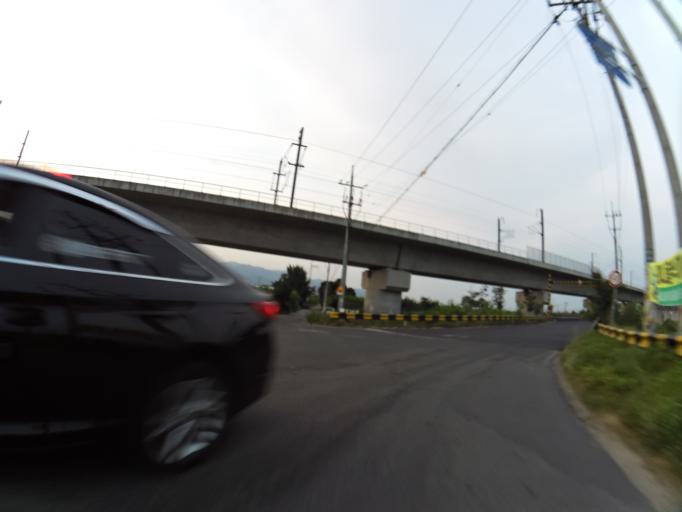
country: KR
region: Gyeongsangbuk-do
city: Gyeongsan-si
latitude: 35.8525
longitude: 128.7482
